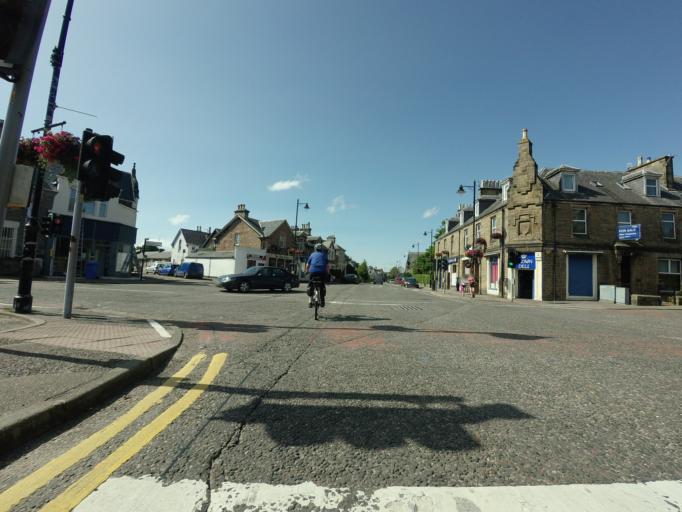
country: GB
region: Scotland
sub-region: Highland
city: Inverness
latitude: 57.4760
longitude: -4.2172
